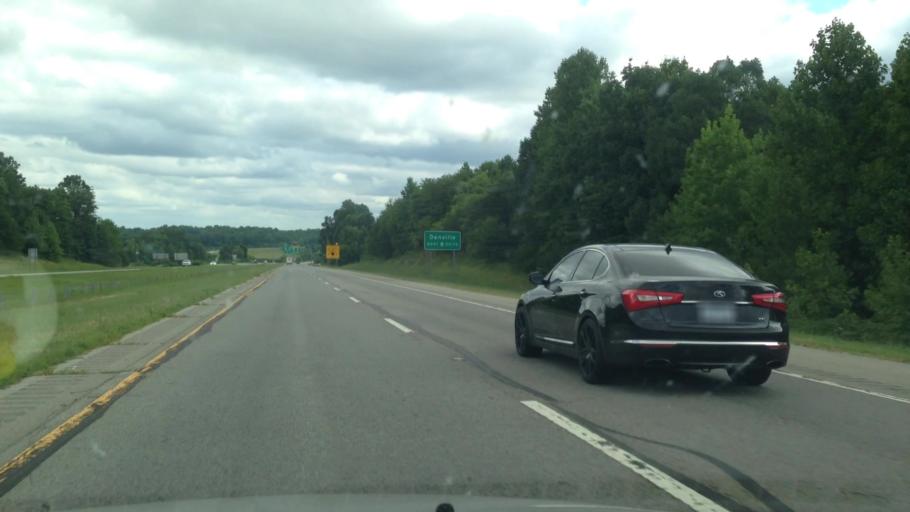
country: US
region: Virginia
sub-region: City of Danville
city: Danville
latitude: 36.5304
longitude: -79.4705
